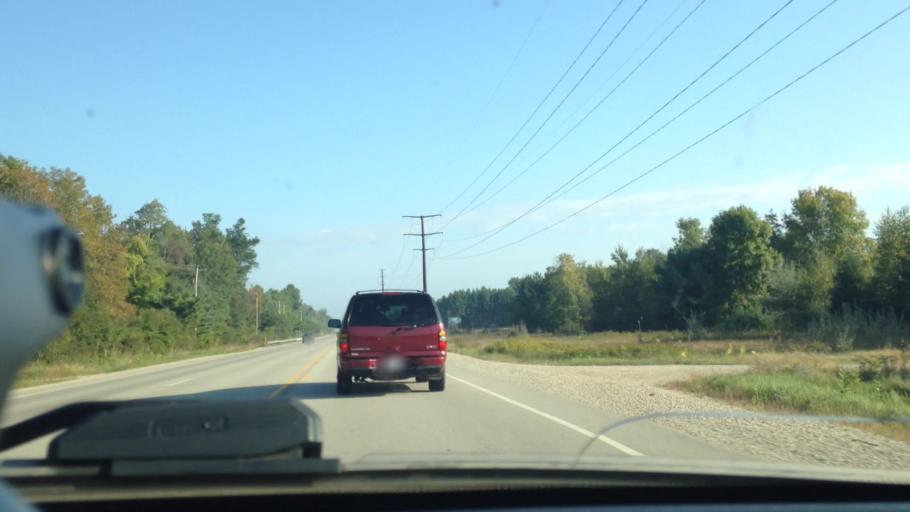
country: US
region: Wisconsin
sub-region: Marinette County
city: Peshtigo
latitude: 45.1840
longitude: -87.9955
